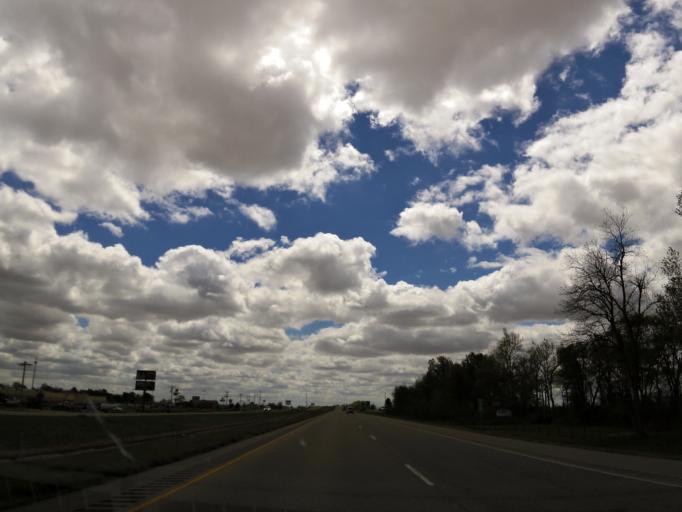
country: US
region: Arkansas
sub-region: Poinsett County
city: Trumann
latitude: 35.6856
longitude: -90.5529
